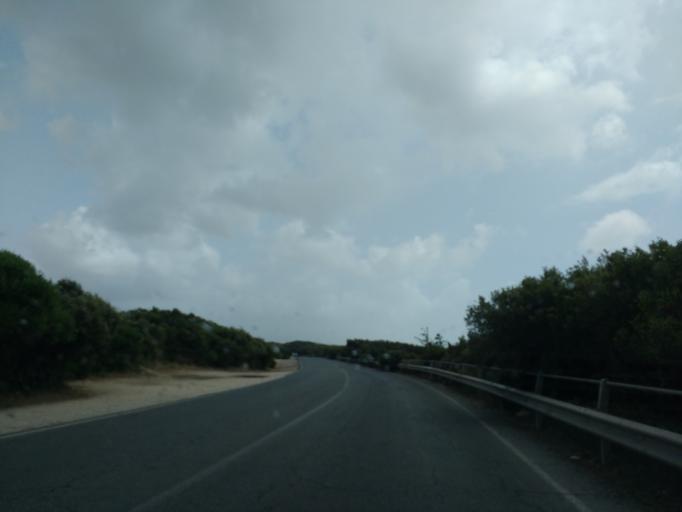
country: IT
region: Latium
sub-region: Citta metropolitana di Roma Capitale
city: Torvaianica
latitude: 41.6693
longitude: 12.3996
